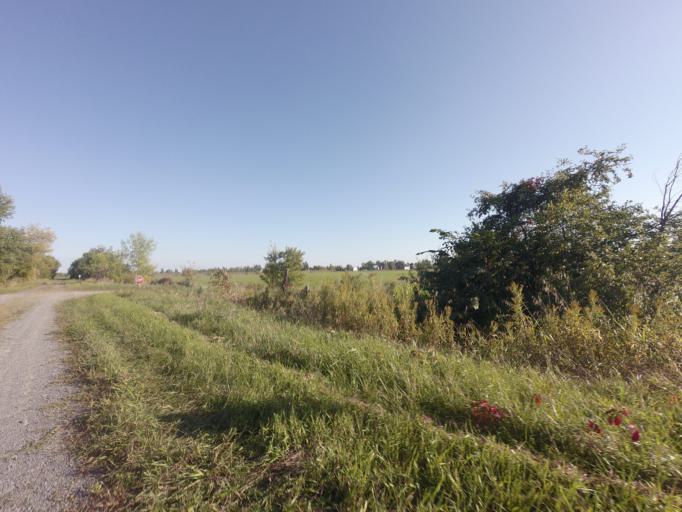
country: CA
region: Ontario
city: Hawkesbury
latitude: 45.5154
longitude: -74.5153
